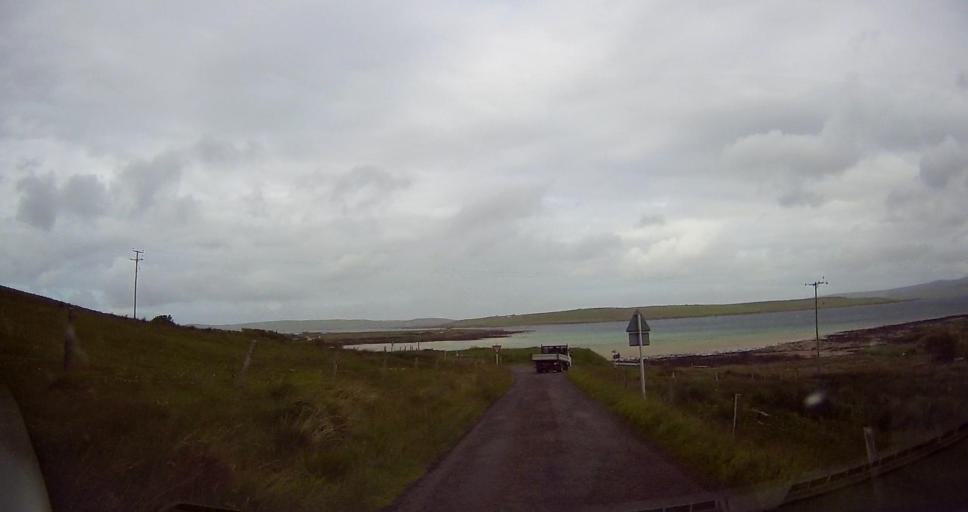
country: GB
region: Scotland
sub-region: Orkney Islands
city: Stromness
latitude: 58.9052
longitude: -3.3166
